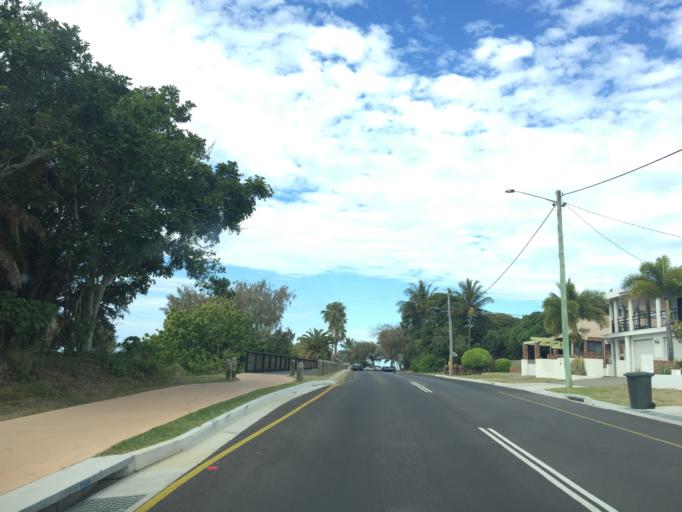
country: AU
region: Queensland
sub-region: Bundaberg
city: Bundaberg
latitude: -24.8268
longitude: 152.4645
